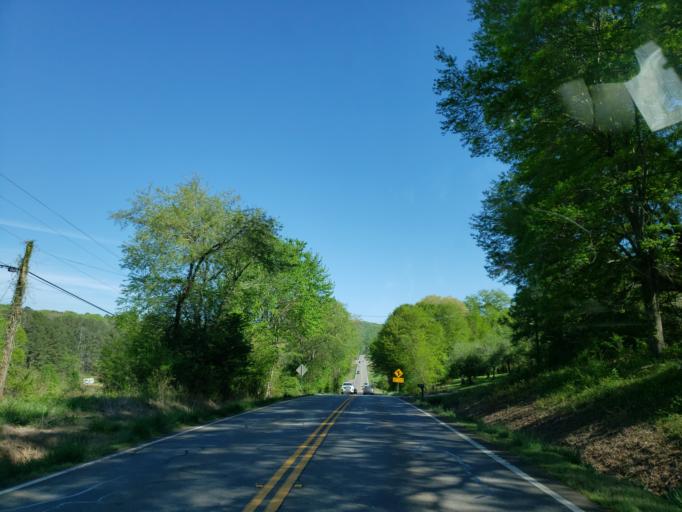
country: US
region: Georgia
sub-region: Cherokee County
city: Canton
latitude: 34.3062
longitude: -84.5283
